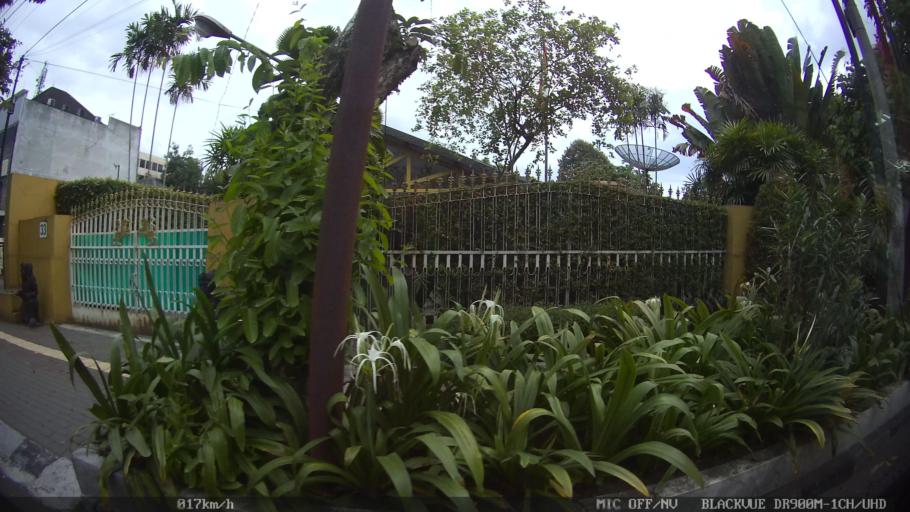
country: ID
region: Daerah Istimewa Yogyakarta
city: Yogyakarta
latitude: -7.7938
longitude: 110.3930
